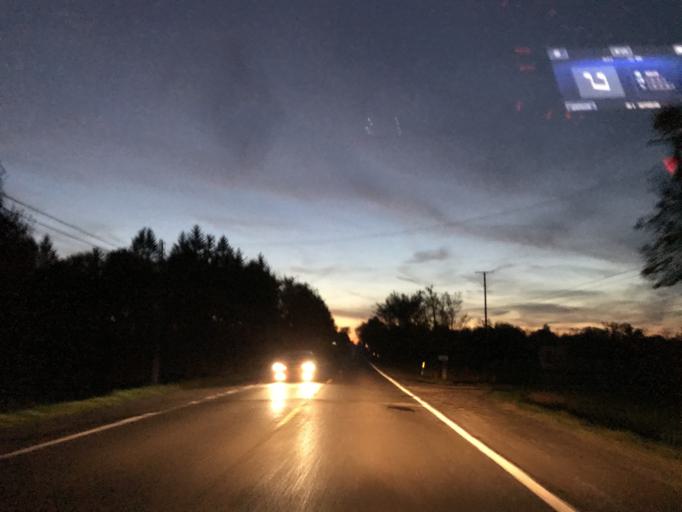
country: US
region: Michigan
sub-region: Oakland County
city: South Lyon
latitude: 42.4341
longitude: -83.5833
